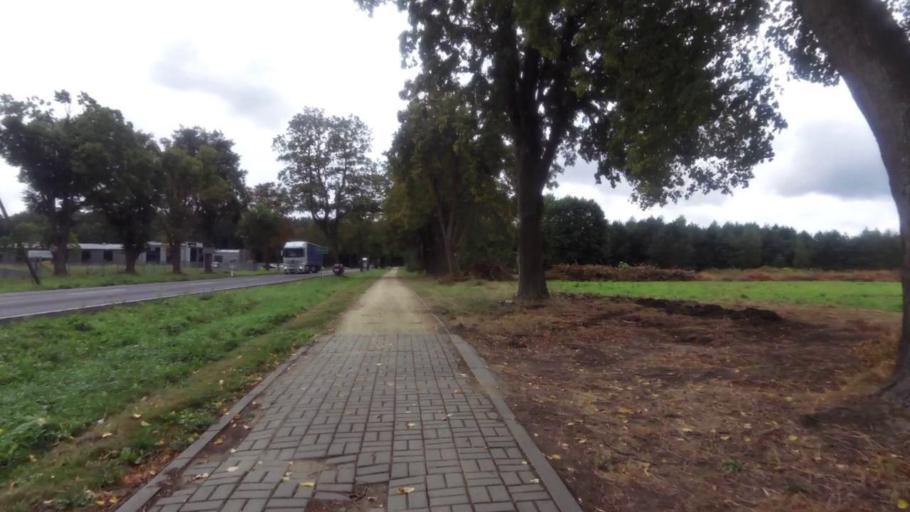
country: PL
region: West Pomeranian Voivodeship
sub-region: Powiat mysliborski
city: Debno
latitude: 52.7241
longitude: 14.6936
